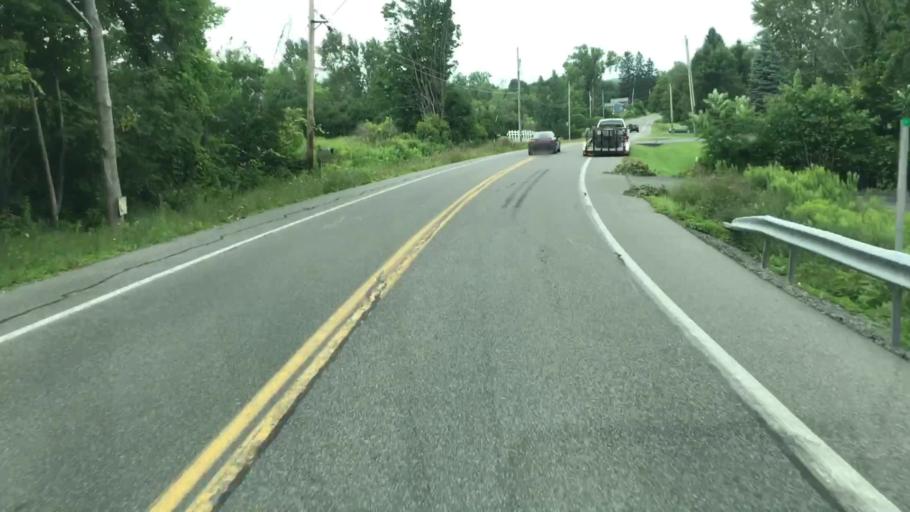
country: US
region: New York
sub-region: Onondaga County
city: Camillus
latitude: 43.0627
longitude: -76.3225
